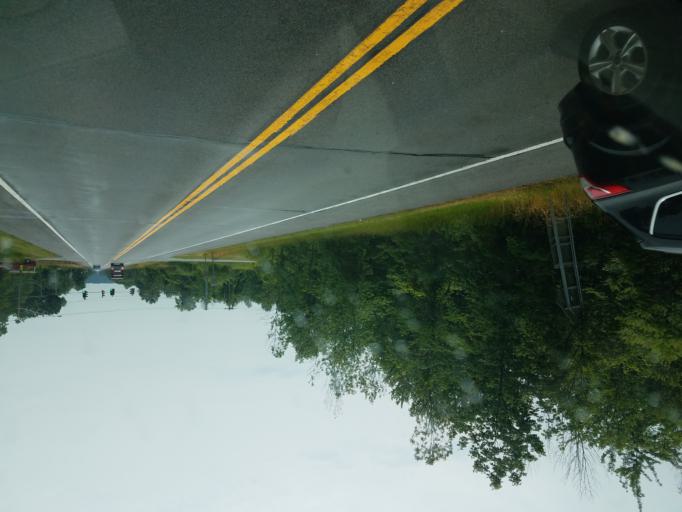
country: US
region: New York
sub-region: Niagara County
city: Lewiston
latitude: 43.2101
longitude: -79.0177
